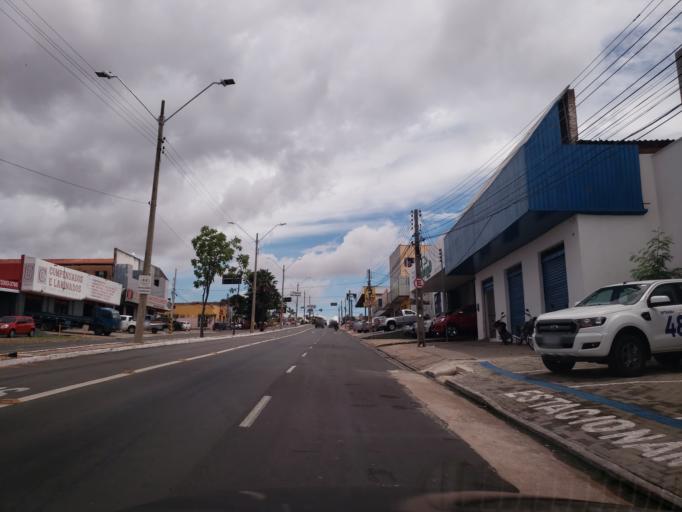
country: BR
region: Piaui
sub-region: Teresina
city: Teresina
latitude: -5.1122
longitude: -42.8064
